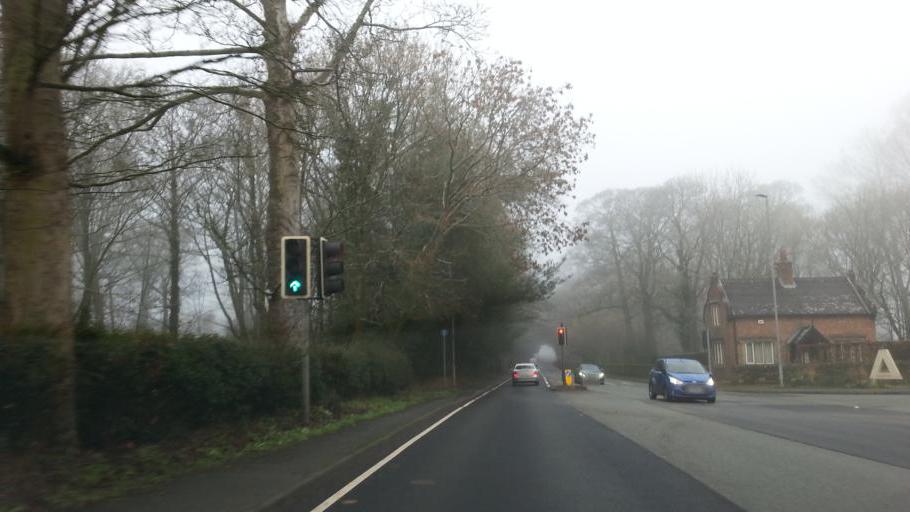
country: GB
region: England
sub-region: Cheshire East
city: Alderley Edge
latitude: 53.2697
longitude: -2.2378
